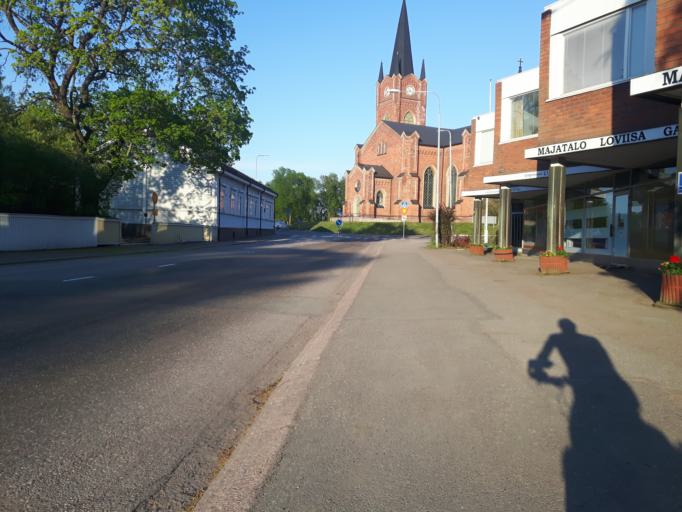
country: FI
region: Uusimaa
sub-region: Loviisa
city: Lovisa
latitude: 60.4565
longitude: 26.2207
